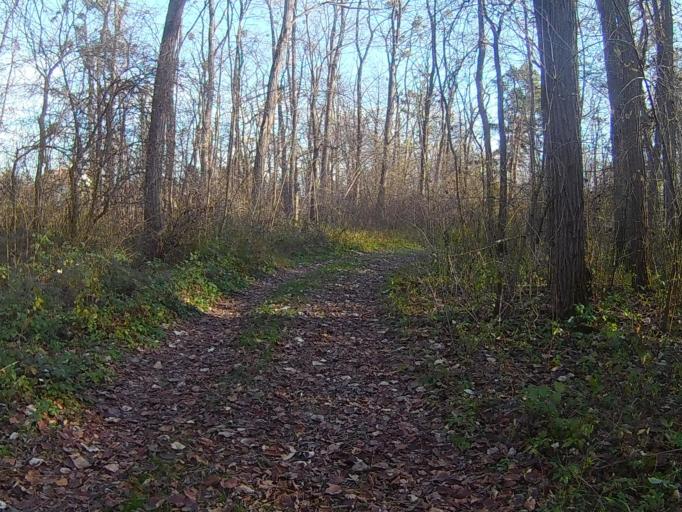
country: SI
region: Duplek
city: Zgornji Duplek
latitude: 46.5099
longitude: 15.7204
